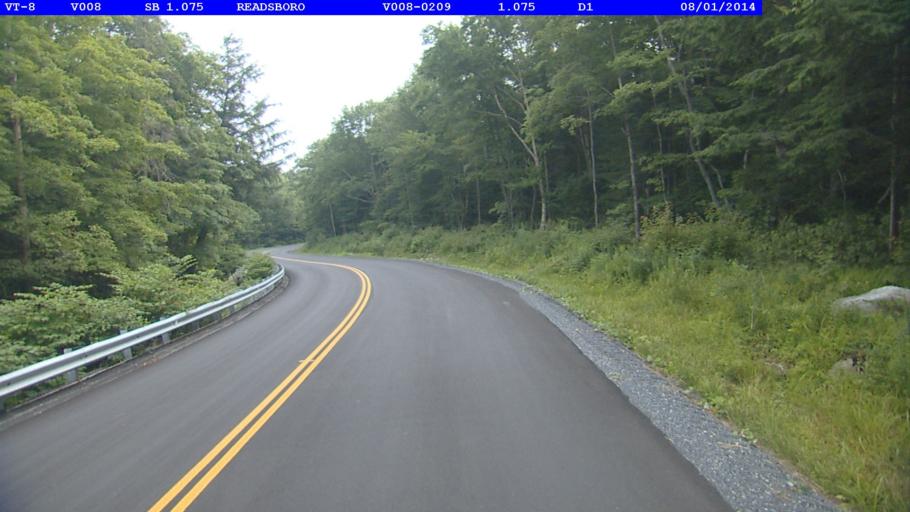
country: US
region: Massachusetts
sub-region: Berkshire County
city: North Adams
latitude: 42.8425
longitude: -72.9925
